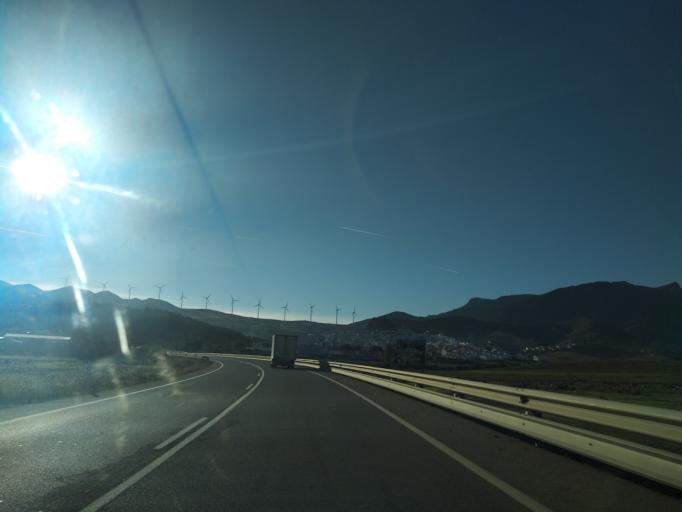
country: ES
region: Andalusia
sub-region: Provincia de Malaga
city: Ardales
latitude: 36.8911
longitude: -4.8480
